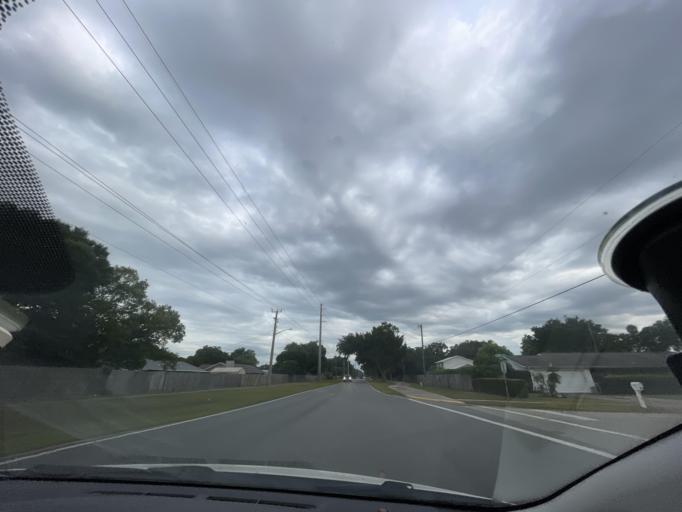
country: US
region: Florida
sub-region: Volusia County
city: Port Orange
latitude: 29.1038
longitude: -80.9932
